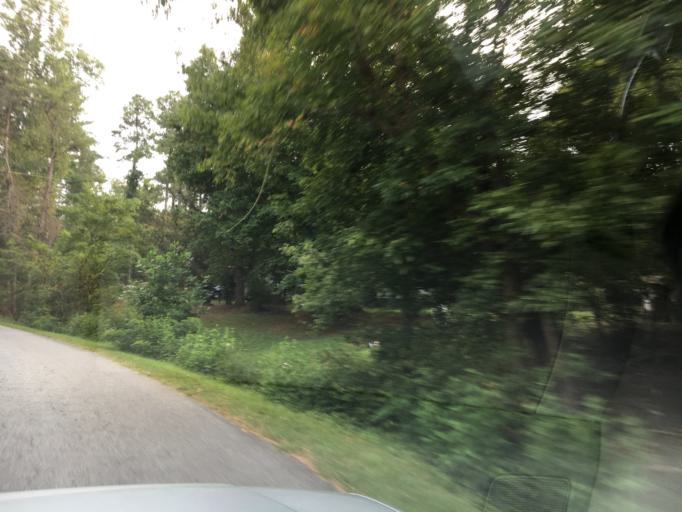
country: US
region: South Carolina
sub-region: Spartanburg County
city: Boiling Springs
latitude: 35.1782
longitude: -82.0337
